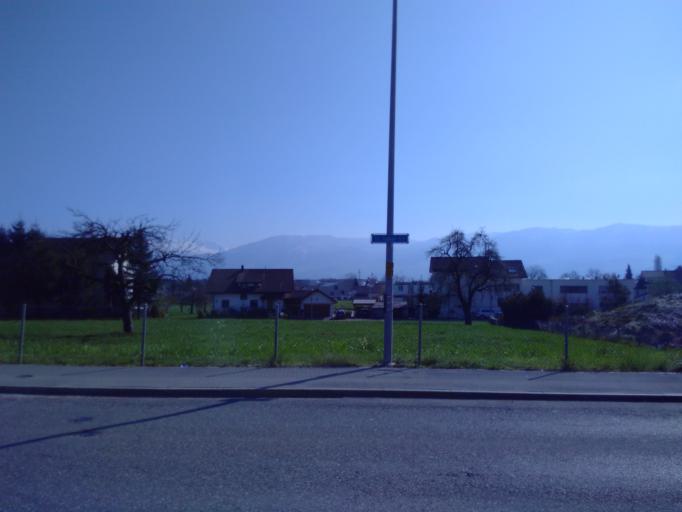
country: CH
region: Saint Gallen
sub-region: Wahlkreis See-Gaster
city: Jona
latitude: 47.2297
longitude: 8.8420
